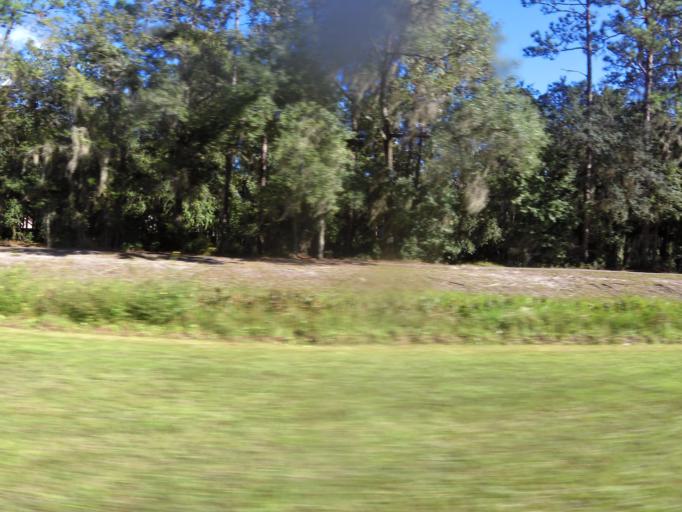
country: US
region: Florida
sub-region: Alachua County
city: Alachua
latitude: 29.7107
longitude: -82.3886
